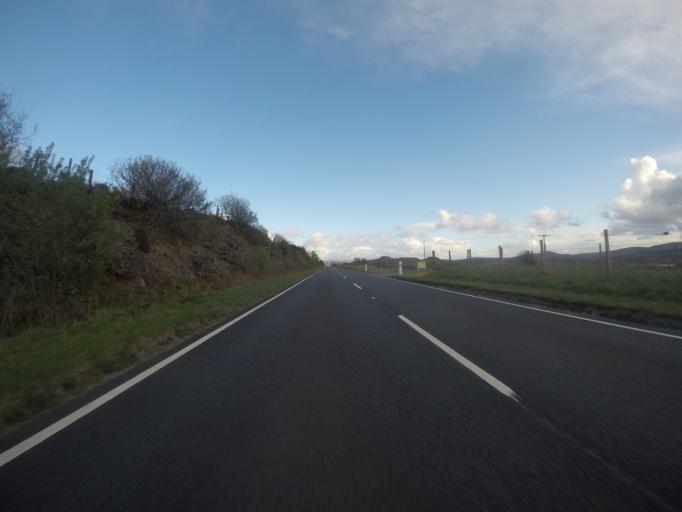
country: GB
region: Scotland
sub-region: Highland
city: Portree
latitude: 57.4965
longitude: -6.3221
